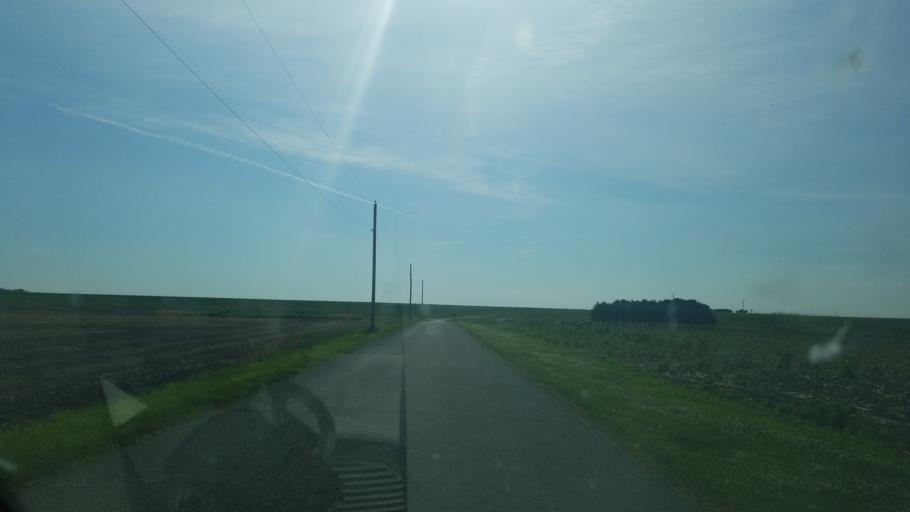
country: US
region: Ohio
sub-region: Hancock County
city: Findlay
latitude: 41.0219
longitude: -83.5854
